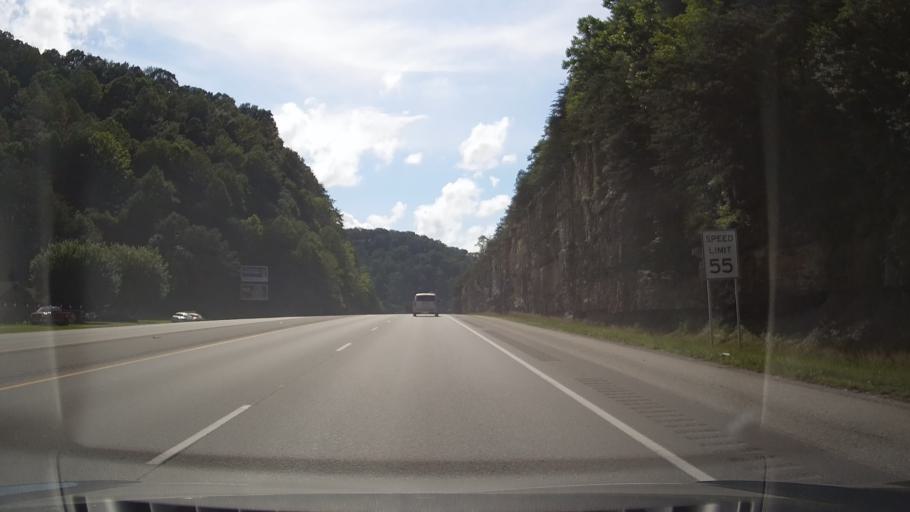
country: US
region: Kentucky
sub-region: Floyd County
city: Prestonsburg
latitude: 37.6438
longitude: -82.7704
